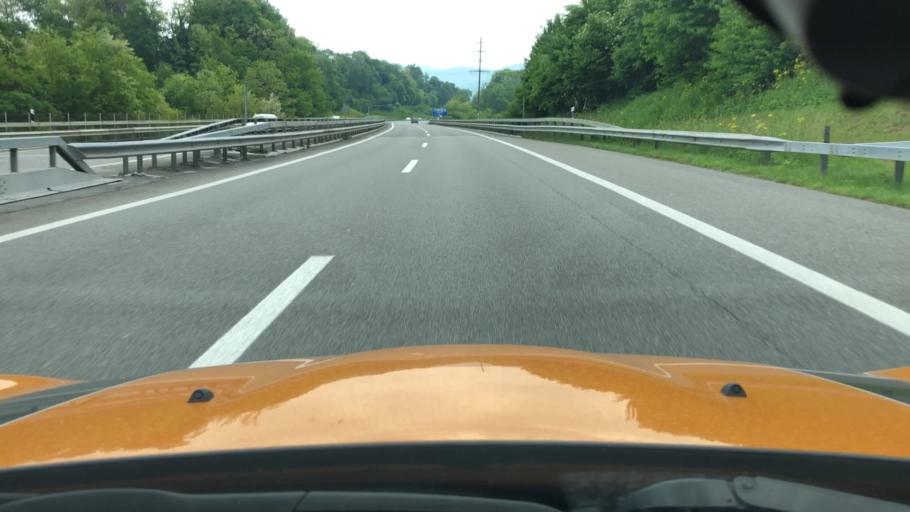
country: CH
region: Ticino
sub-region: Mendrisio District
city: Mendrisio
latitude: 45.8570
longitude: 8.9749
